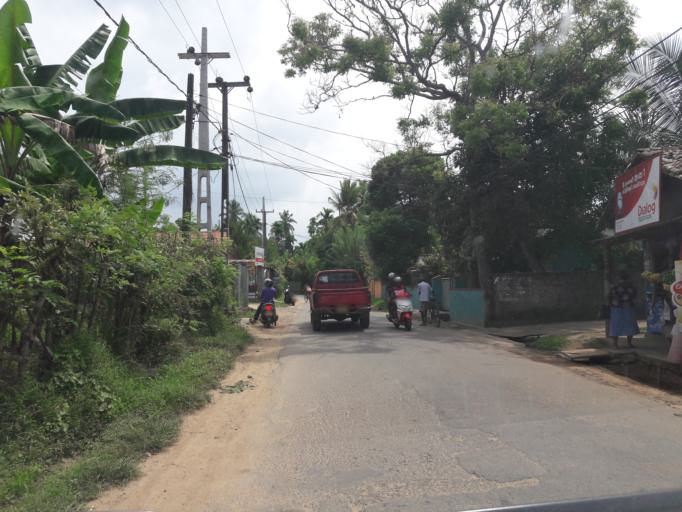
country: LK
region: Southern
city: Hikkaduwa
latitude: 6.0954
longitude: 80.1503
